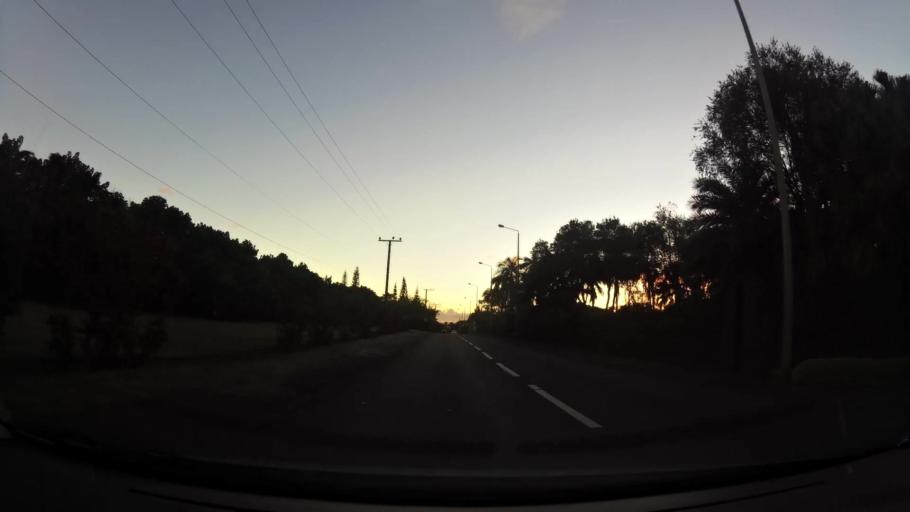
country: MU
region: Moka
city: Saint Pierre
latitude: -20.2238
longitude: 57.5169
